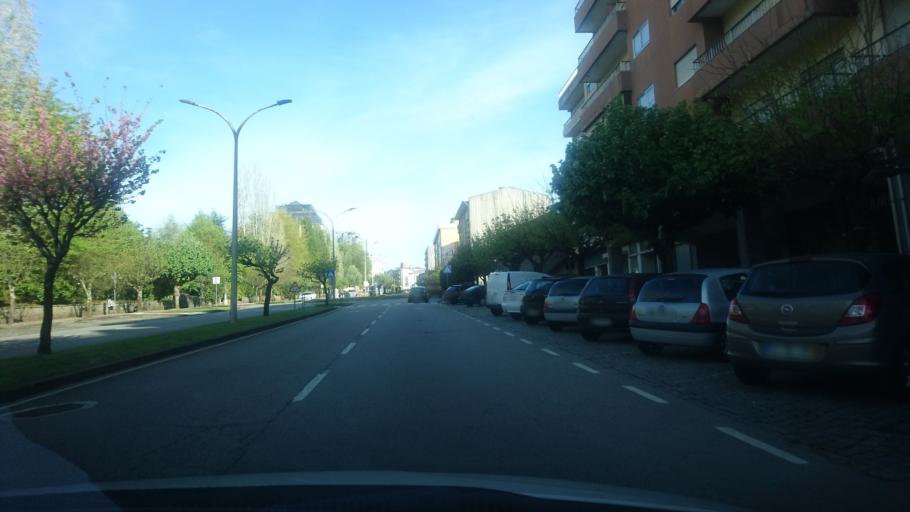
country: PT
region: Aveiro
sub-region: Sao Joao da Madeira
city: Sao Joao da Madeira
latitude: 40.8962
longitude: -8.4861
